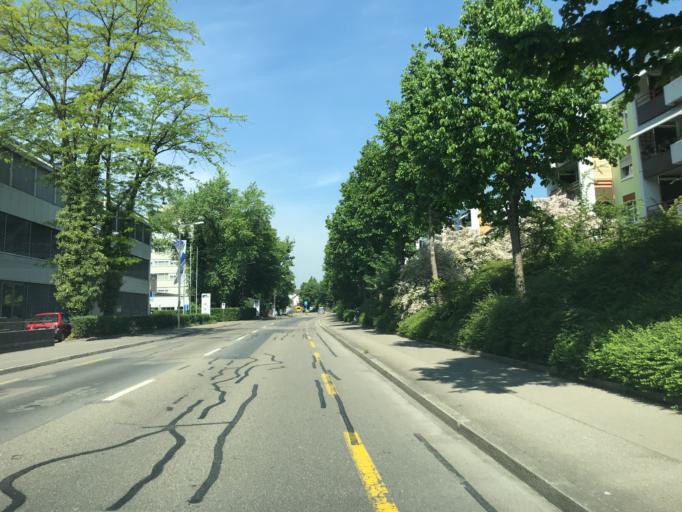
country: CH
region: Zurich
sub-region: Bezirk Winterthur
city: Wuelflingen (Kreis 6) / Oberfeld
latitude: 47.5002
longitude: 8.6942
